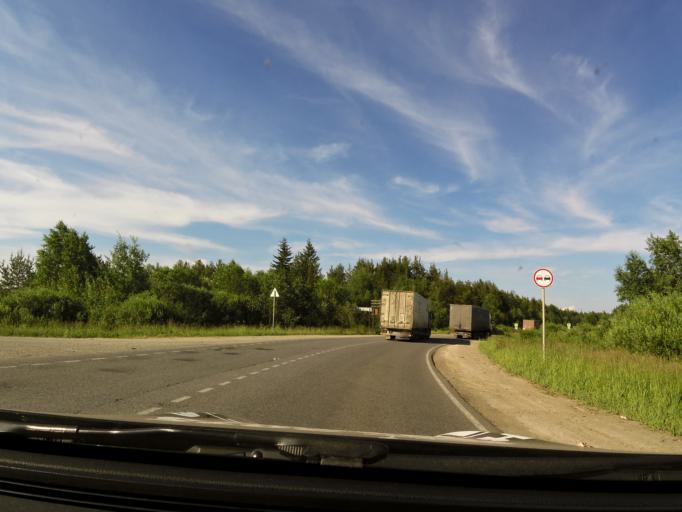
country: RU
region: Kirov
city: Belaya Kholunitsa
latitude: 58.8695
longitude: 50.8439
